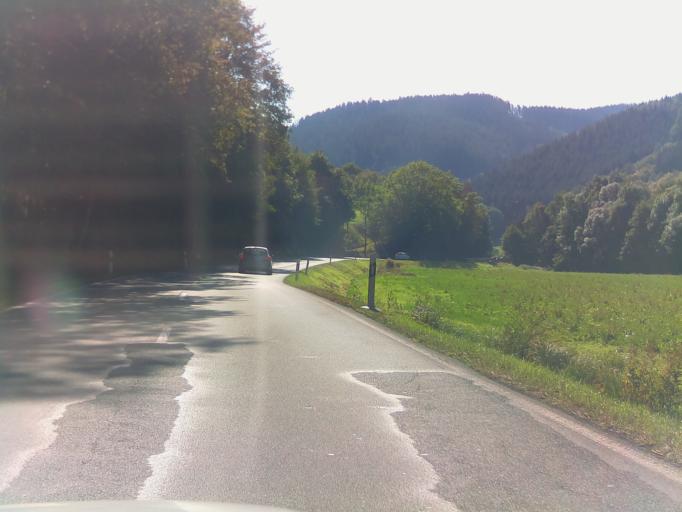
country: DE
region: Thuringia
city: Leutenberg
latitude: 50.5825
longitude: 11.4407
